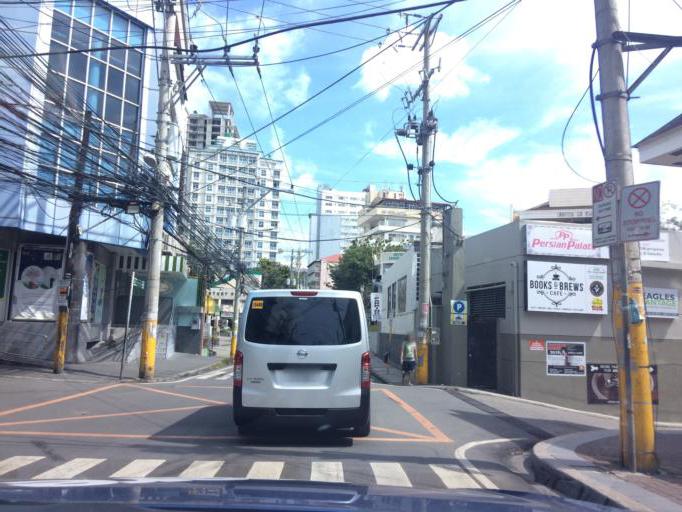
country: PH
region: Central Visayas
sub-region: Province of Cebu
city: Cebu City
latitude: 10.3108
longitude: 123.8953
